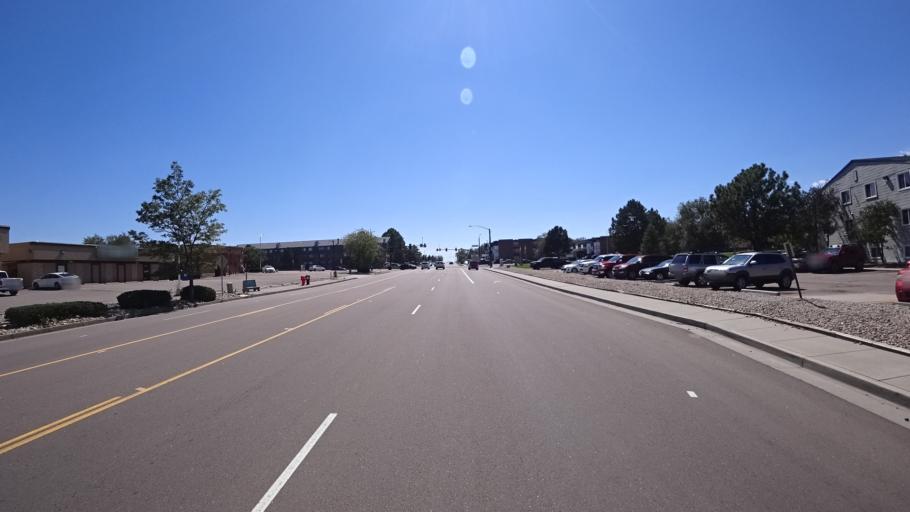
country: US
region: Colorado
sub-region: El Paso County
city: Stratmoor
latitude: 38.8161
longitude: -104.7664
